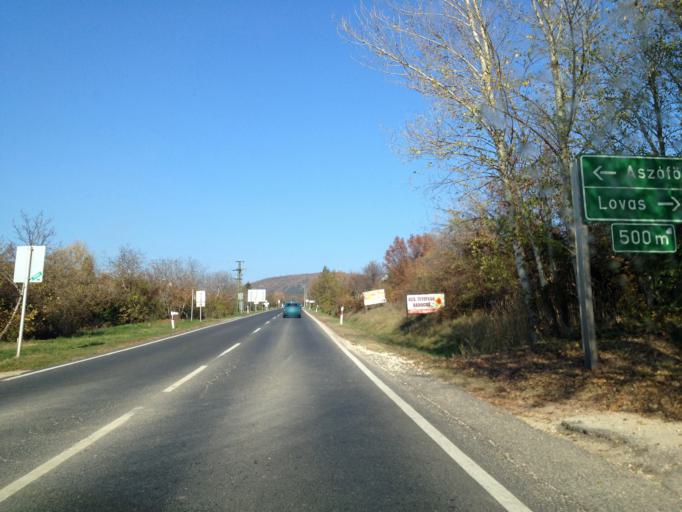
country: HU
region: Veszprem
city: Csopak
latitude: 46.9737
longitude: 17.9165
